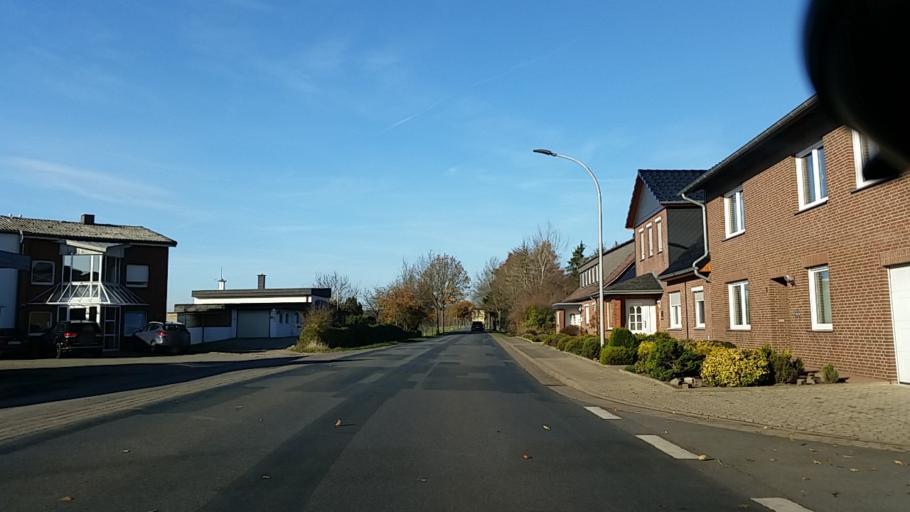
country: DE
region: Saxony-Anhalt
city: Jubar
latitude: 52.6733
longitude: 10.8468
